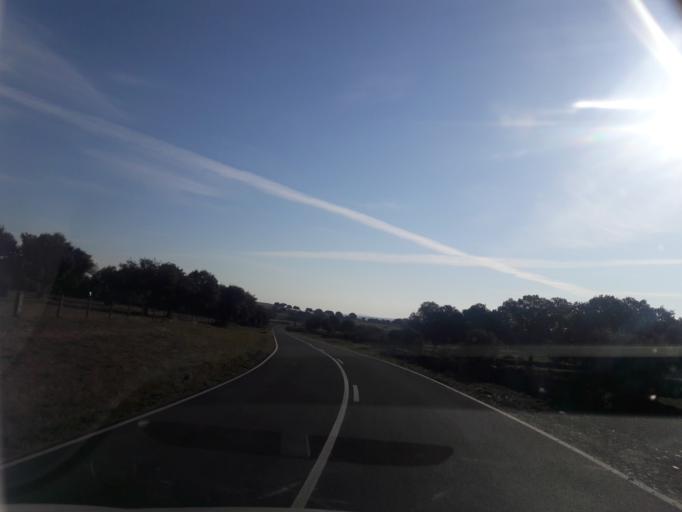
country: ES
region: Castille and Leon
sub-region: Provincia de Salamanca
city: Aldeavieja de Tormes
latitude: 40.5771
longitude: -5.6342
